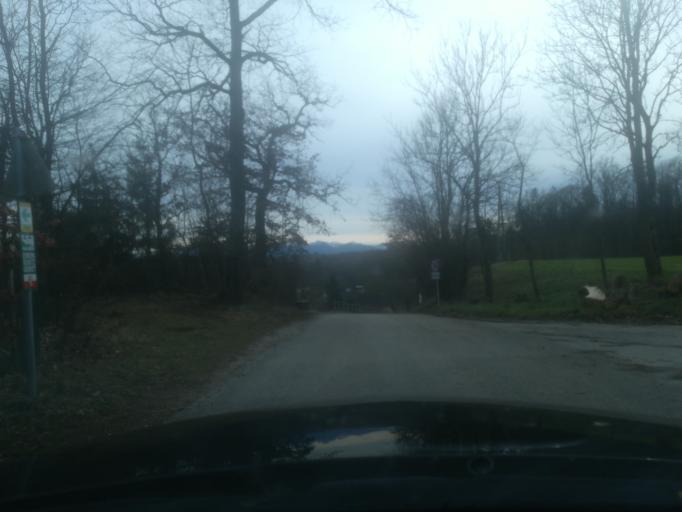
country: AT
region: Upper Austria
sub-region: Wels-Land
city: Gunskirchen
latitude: 48.1106
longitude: 13.9394
